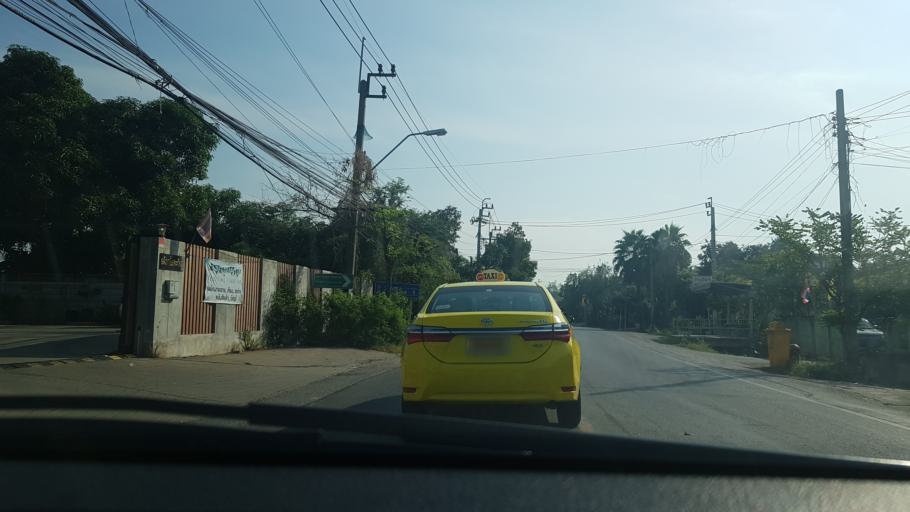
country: TH
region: Bangkok
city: Thawi Watthana
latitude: 13.7989
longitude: 100.3669
